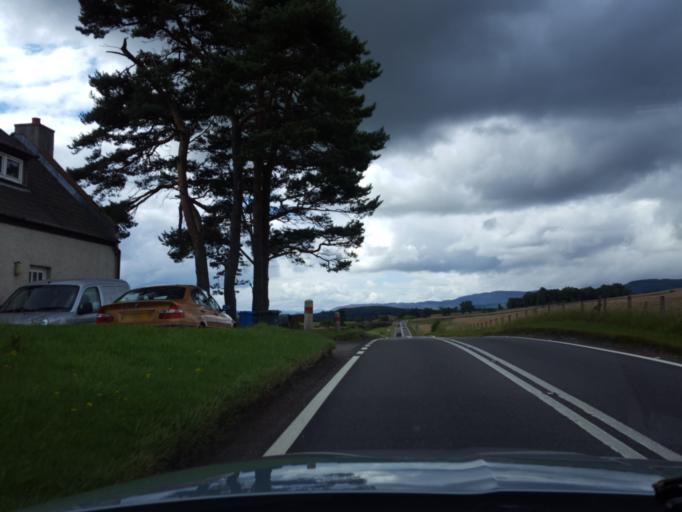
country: GB
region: Scotland
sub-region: Highland
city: Grantown on Spey
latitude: 57.2688
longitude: -3.7240
